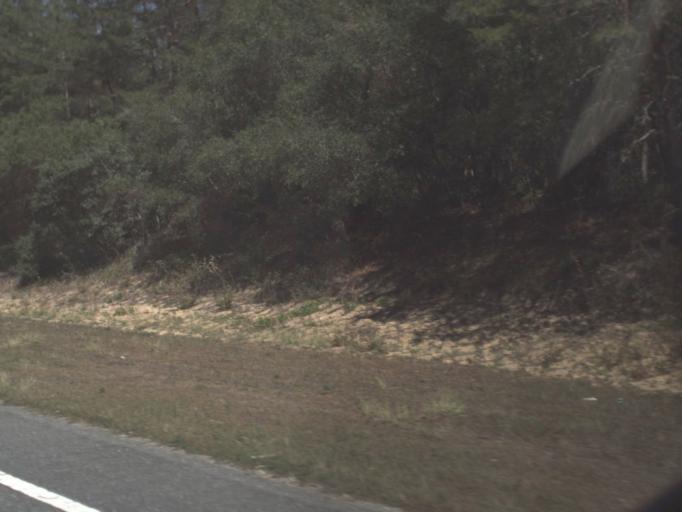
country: US
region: Florida
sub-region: Lake County
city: Astor
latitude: 29.1780
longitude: -81.7303
